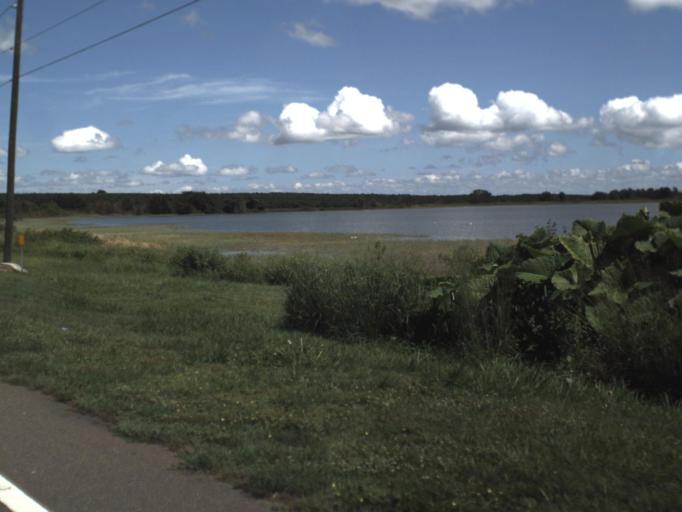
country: US
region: Florida
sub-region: Polk County
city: Frostproof
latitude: 27.7793
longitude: -81.5385
